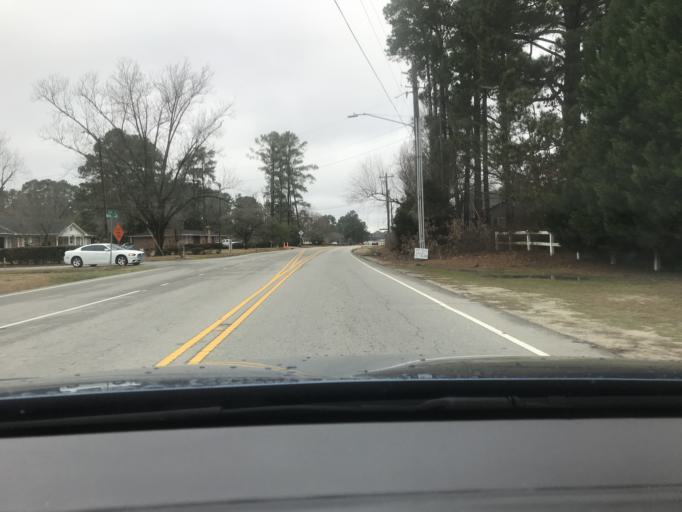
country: US
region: North Carolina
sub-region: Hoke County
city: Rockfish
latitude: 35.0324
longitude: -79.0063
